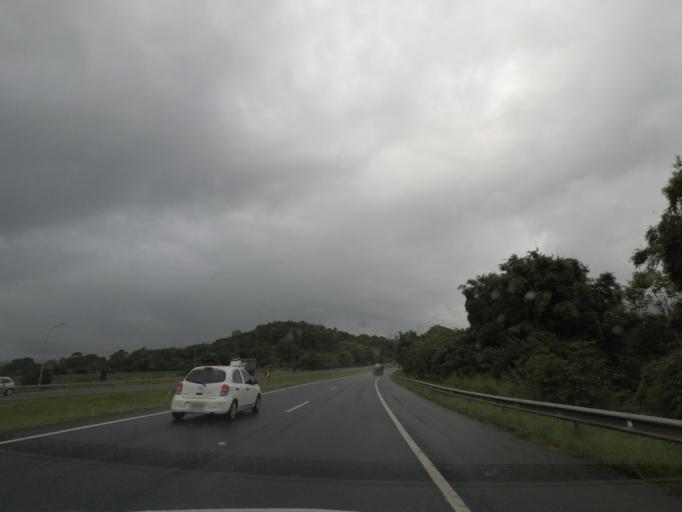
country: BR
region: Sao Paulo
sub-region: Juquia
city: Juquia
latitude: -24.3297
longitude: -47.6207
